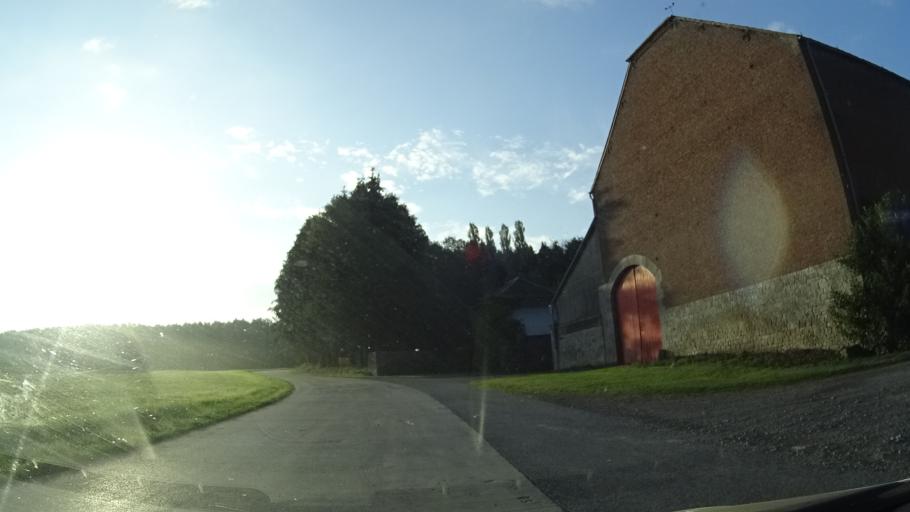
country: BE
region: Wallonia
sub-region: Province du Hainaut
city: Froidchapelle
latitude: 50.2182
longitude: 4.3392
